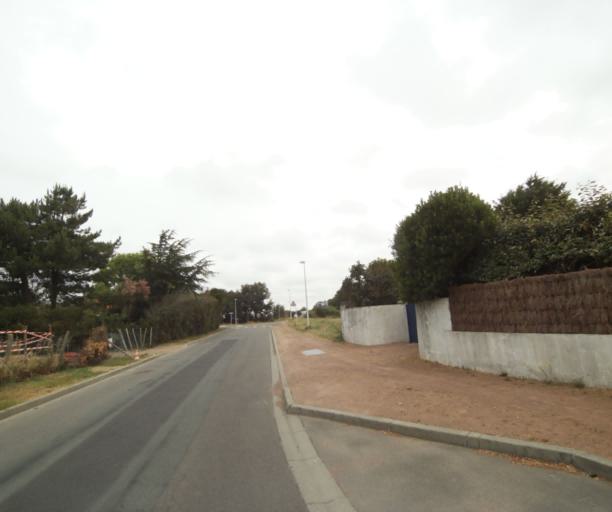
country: FR
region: Pays de la Loire
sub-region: Departement de la Vendee
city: Chateau-d'Olonne
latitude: 46.4821
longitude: -1.7329
